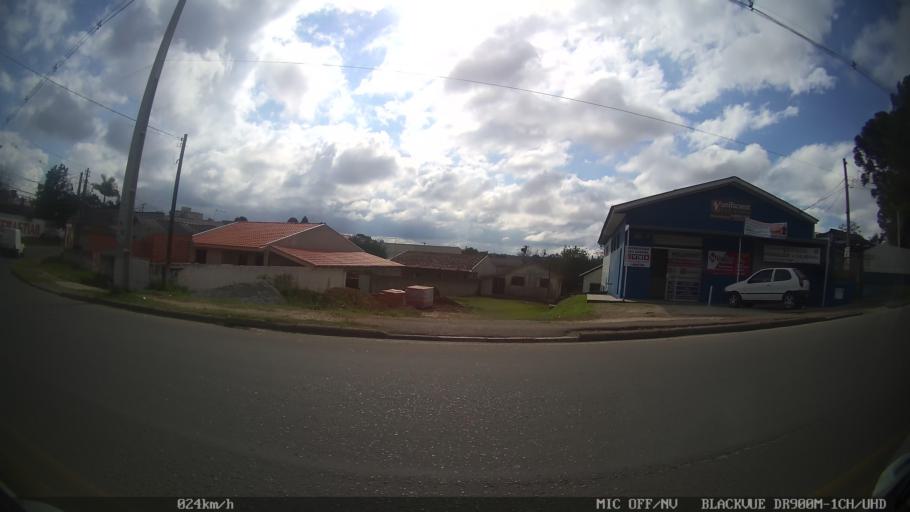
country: BR
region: Parana
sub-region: Colombo
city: Colombo
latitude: -25.3460
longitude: -49.1932
